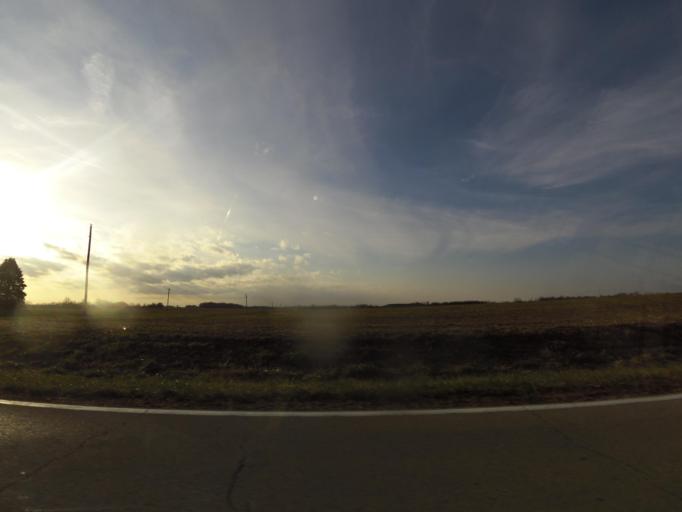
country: US
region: Illinois
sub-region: Fayette County
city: Vandalia
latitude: 38.9208
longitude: -89.2216
